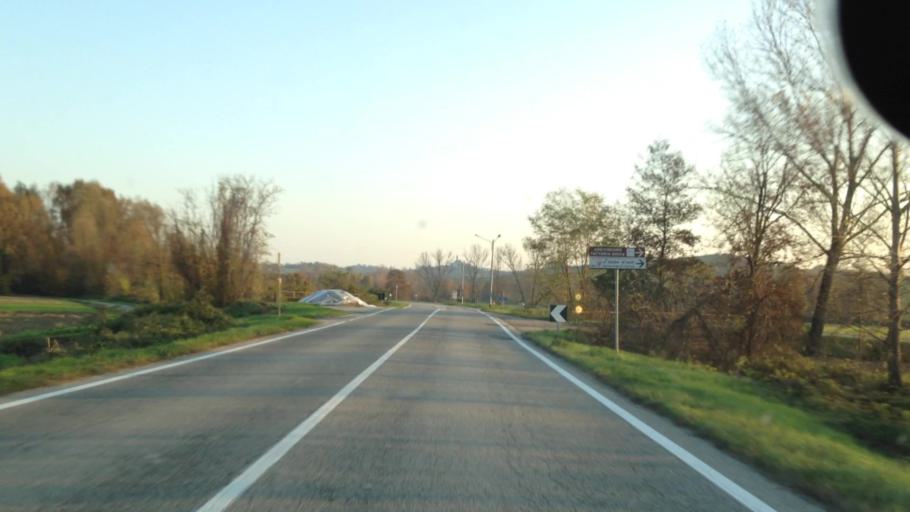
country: IT
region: Piedmont
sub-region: Provincia di Asti
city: Cunico
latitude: 45.0358
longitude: 8.1140
